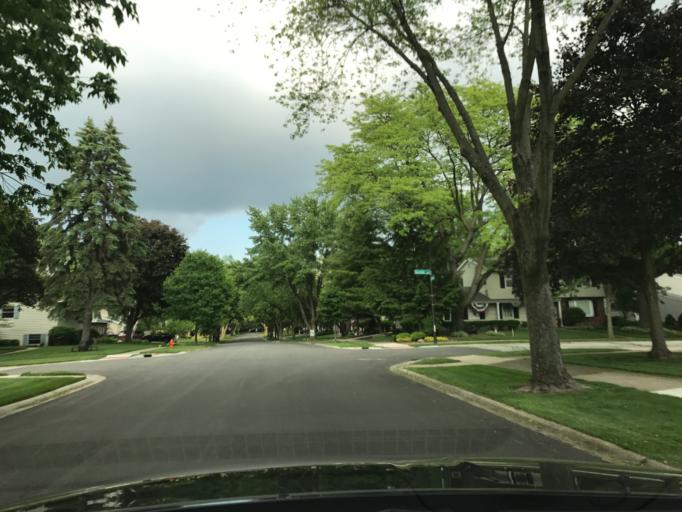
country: US
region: Illinois
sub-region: DuPage County
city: Naperville
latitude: 41.7722
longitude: -88.1280
